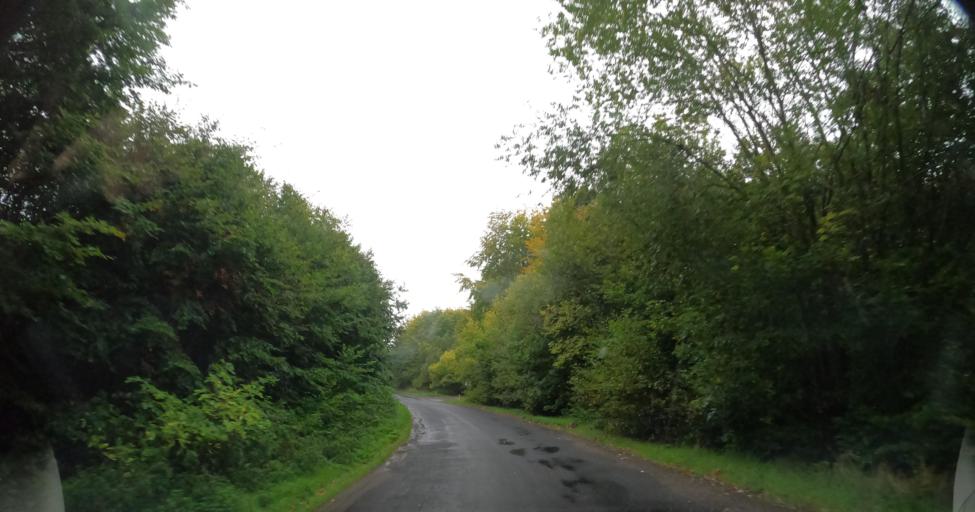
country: PL
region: West Pomeranian Voivodeship
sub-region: Powiat gryfinski
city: Banie
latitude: 53.0534
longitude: 14.7408
